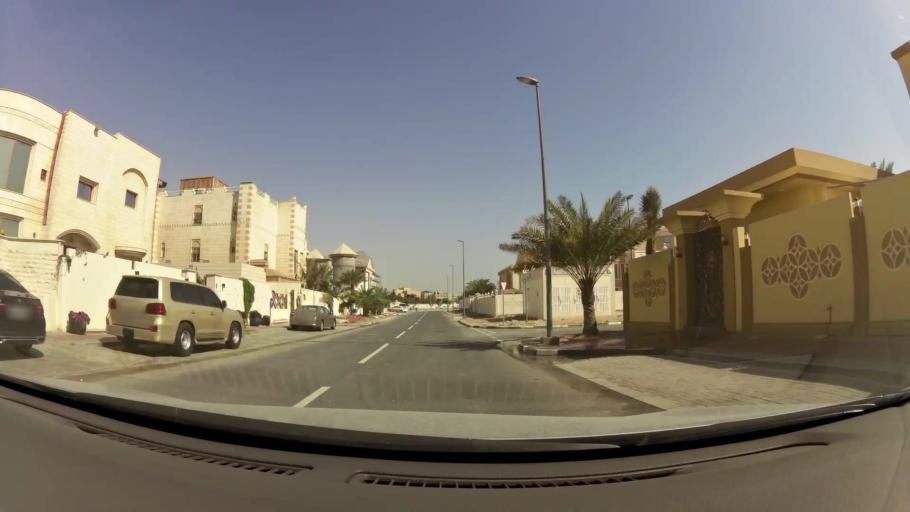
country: QA
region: Baladiyat ad Dawhah
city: Doha
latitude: 25.3628
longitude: 51.5162
